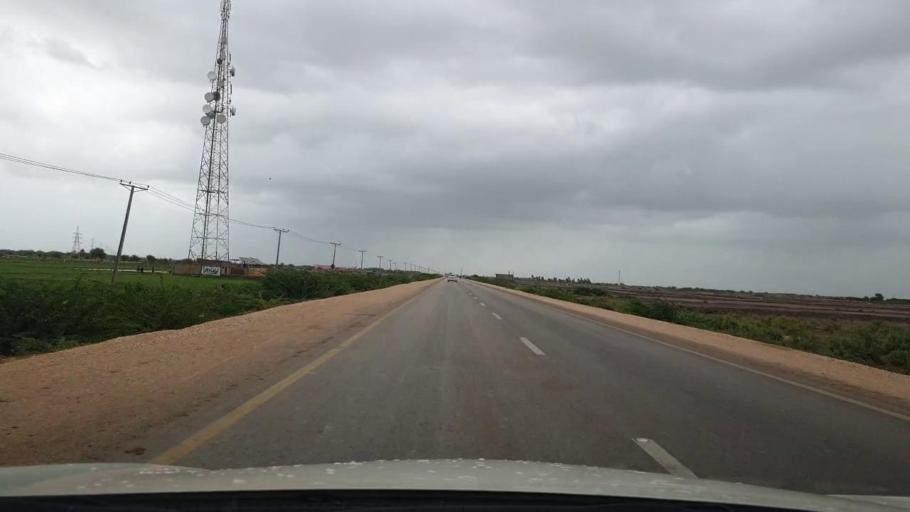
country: PK
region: Sindh
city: Badin
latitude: 24.6548
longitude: 68.7468
